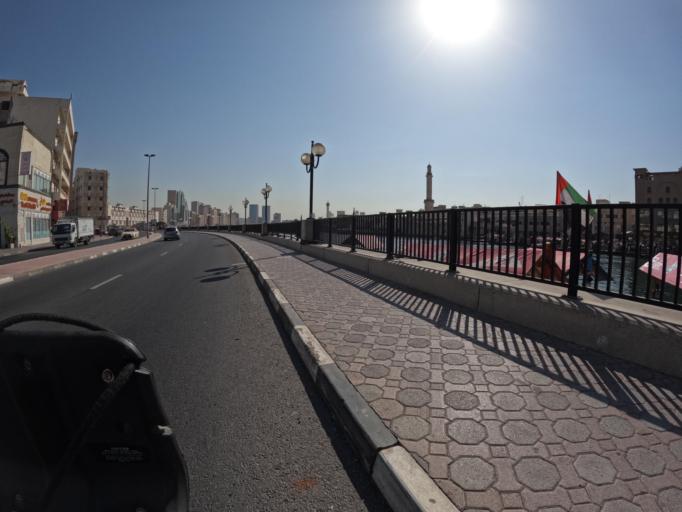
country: AE
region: Ash Shariqah
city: Sharjah
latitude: 25.2655
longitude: 55.2945
